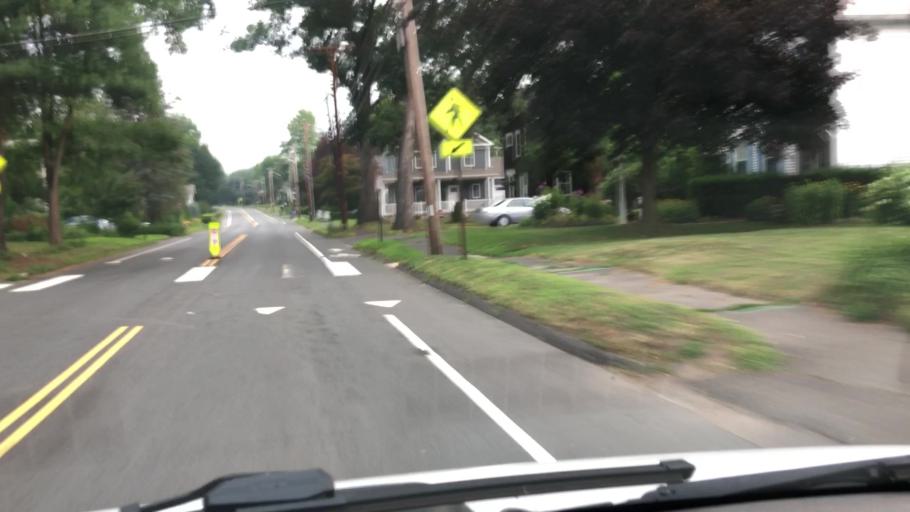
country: US
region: Massachusetts
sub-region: Hampshire County
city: Northampton
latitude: 42.3378
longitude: -72.6750
